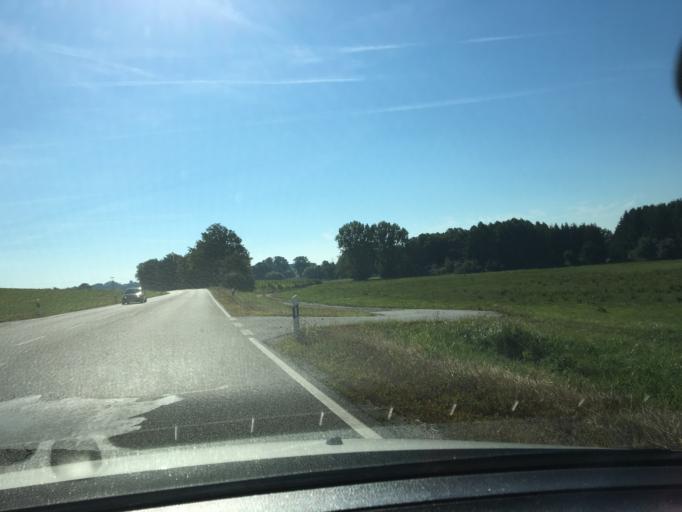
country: DE
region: Bavaria
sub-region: Upper Bavaria
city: Aham
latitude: 48.3515
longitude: 12.1882
